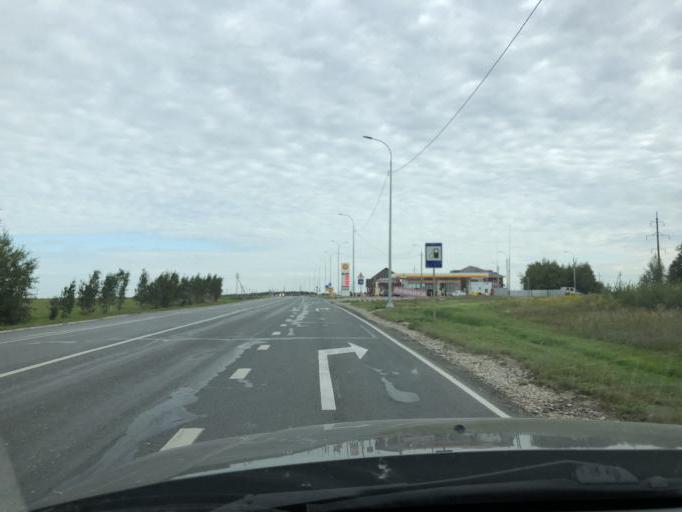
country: RU
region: Tula
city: Barsuki
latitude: 54.2539
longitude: 37.5275
